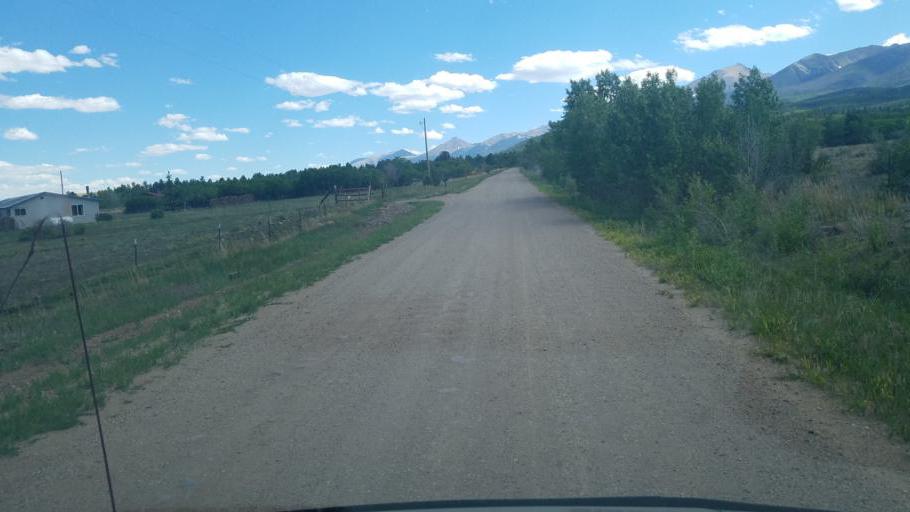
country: US
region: Colorado
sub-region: Custer County
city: Westcliffe
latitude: 38.2302
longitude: -105.5990
